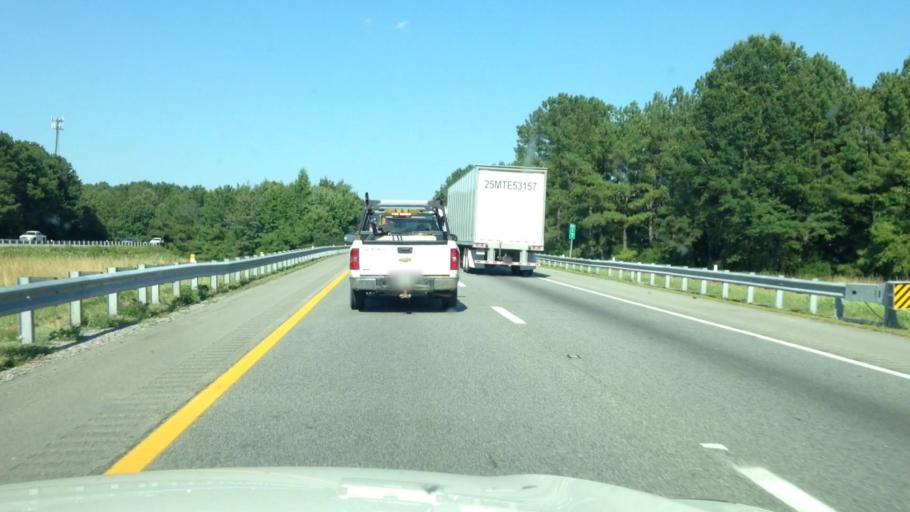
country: US
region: Virginia
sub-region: City of Emporia
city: Emporia
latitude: 36.7649
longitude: -77.4822
